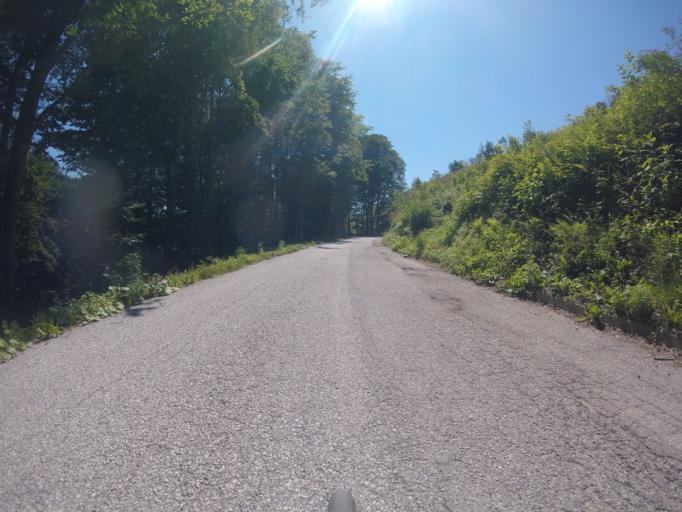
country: SI
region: Kostanjevica na Krki
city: Kostanjevica na Krki
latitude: 45.8150
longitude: 15.5111
